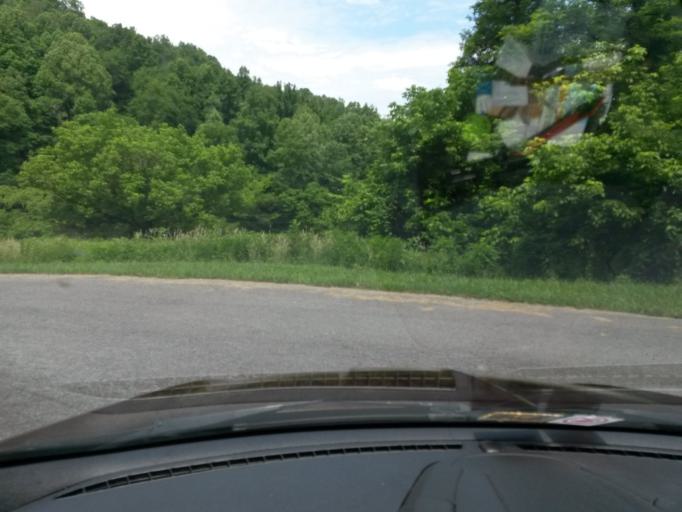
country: US
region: West Virginia
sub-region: Lewis County
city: Weston
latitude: 39.0096
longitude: -80.4687
